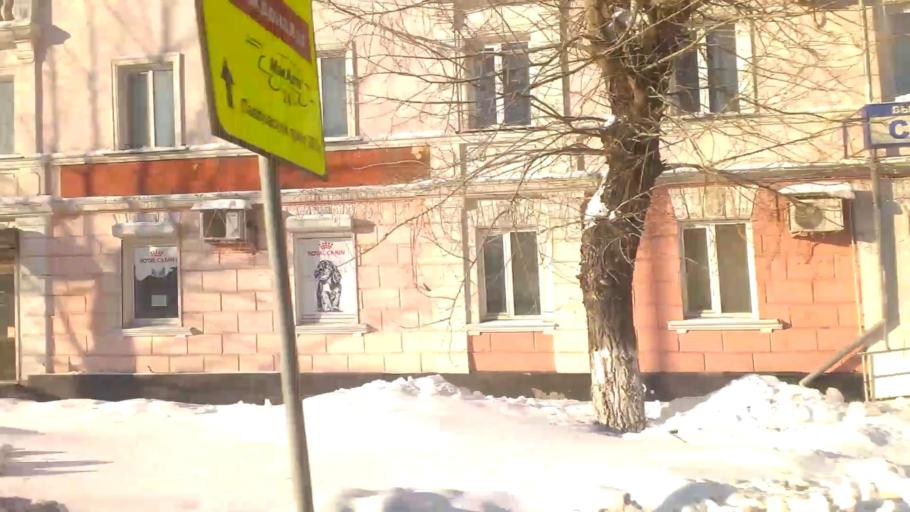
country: RU
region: Altai Krai
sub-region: Gorod Barnaulskiy
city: Barnaul
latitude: 53.3475
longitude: 83.7598
